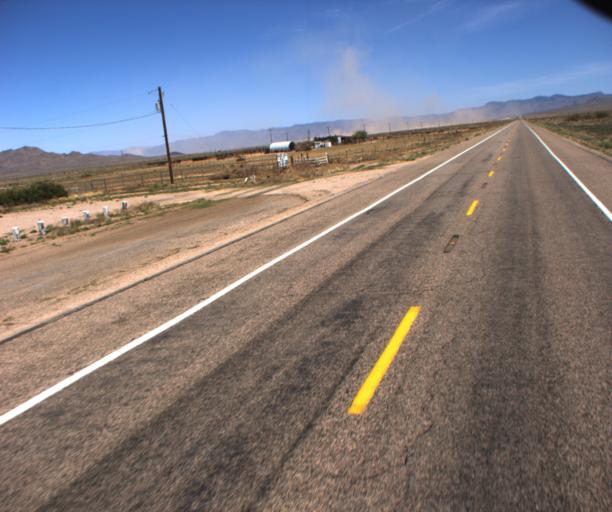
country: US
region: Arizona
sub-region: Mohave County
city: New Kingman-Butler
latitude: 35.3087
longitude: -113.9233
